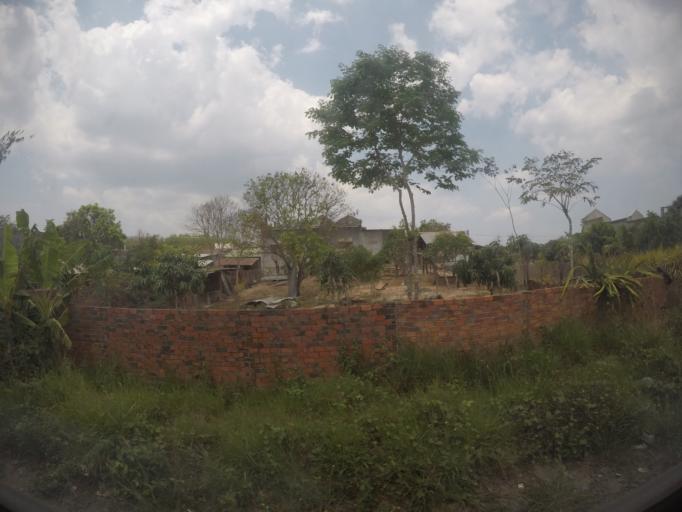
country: VN
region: Binh Thuan
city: Tanh Linh
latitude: 10.9446
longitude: 107.6571
